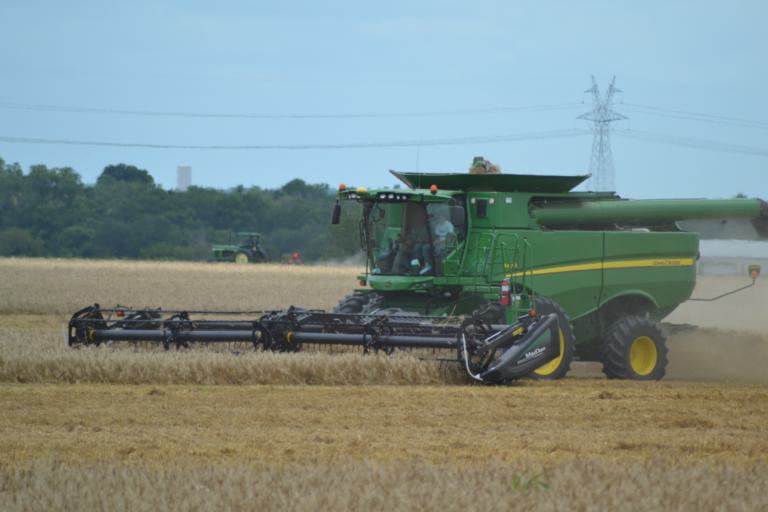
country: US
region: Texas
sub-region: Bell County
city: Rogers
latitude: 30.9969
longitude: -97.1500
